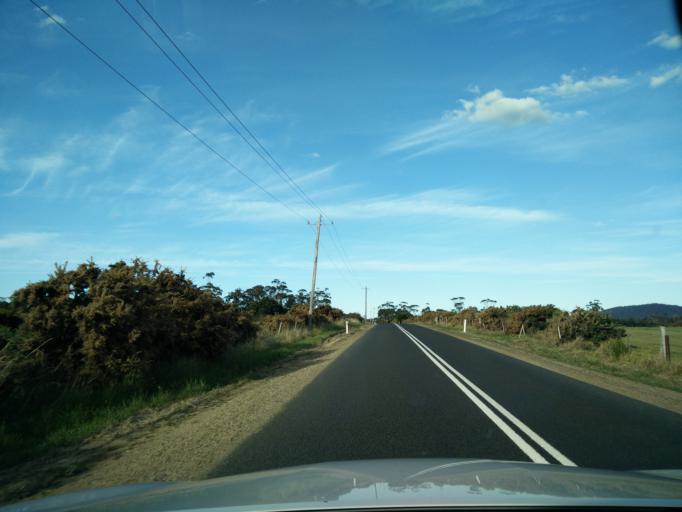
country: AU
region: Tasmania
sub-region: Break O'Day
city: St Helens
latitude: -41.9245
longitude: 148.2379
